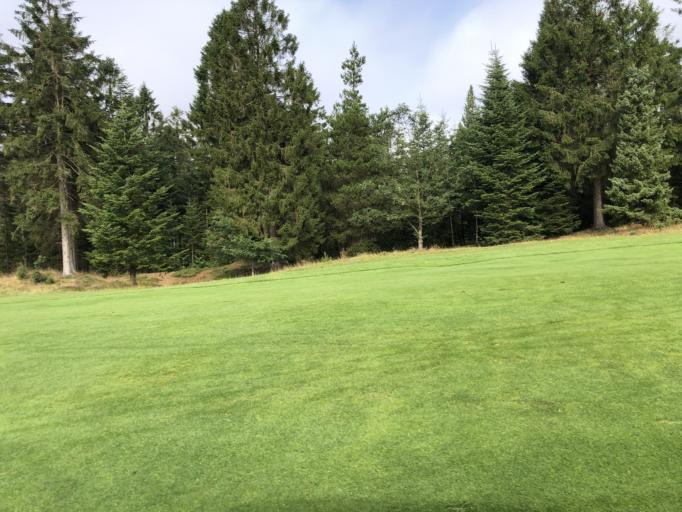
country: DK
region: Central Jutland
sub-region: Holstebro Kommune
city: Ulfborg
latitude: 56.3263
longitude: 8.4222
